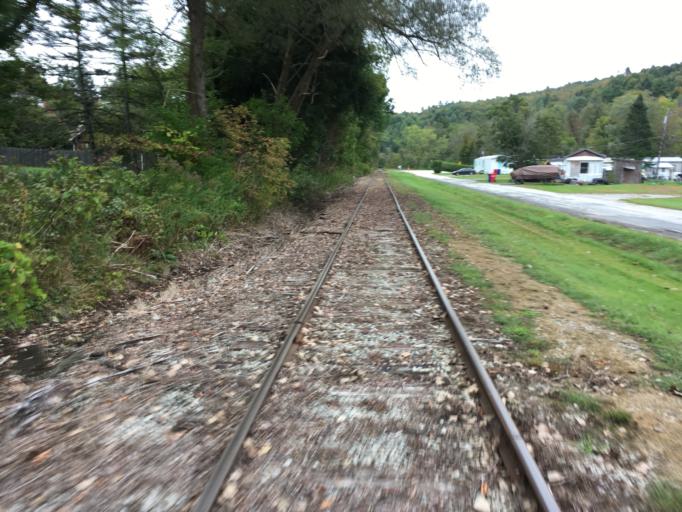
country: US
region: Vermont
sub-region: Washington County
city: Barre
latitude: 44.2169
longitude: -72.5386
